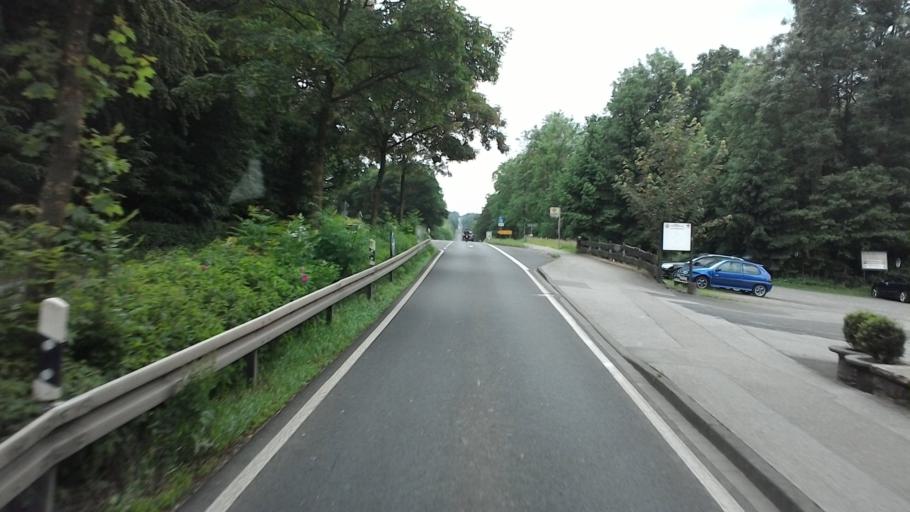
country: DE
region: North Rhine-Westphalia
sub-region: Regierungsbezirk Koln
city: Roetgen
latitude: 50.6827
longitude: 6.1807
